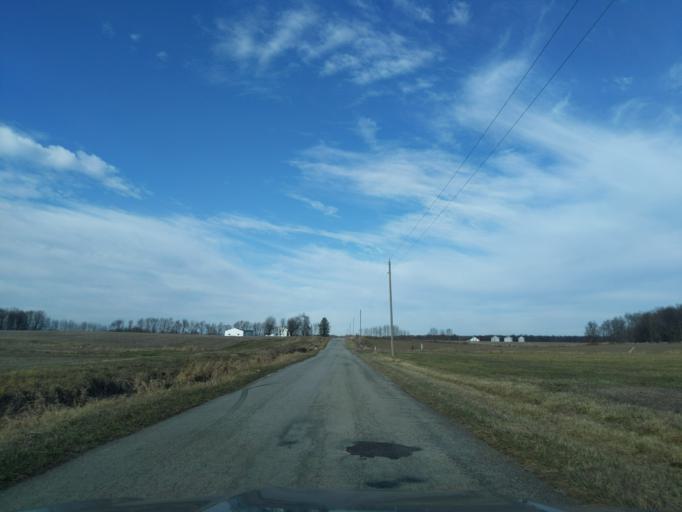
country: US
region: Indiana
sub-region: Decatur County
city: Greensburg
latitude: 39.2546
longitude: -85.4190
